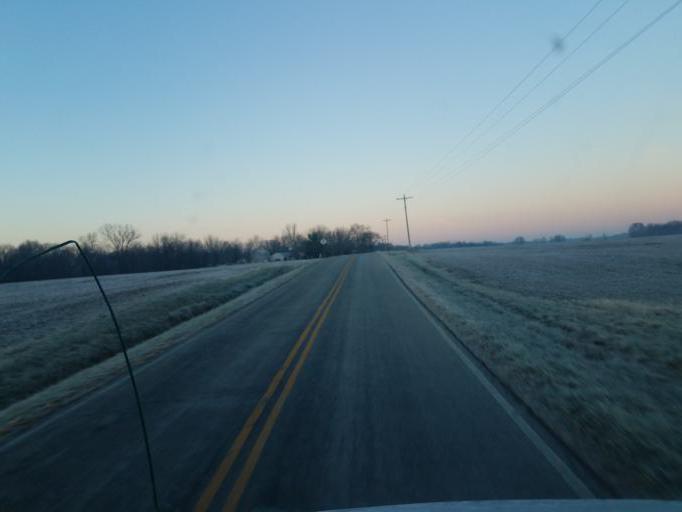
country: US
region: Ohio
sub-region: Marion County
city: Marion
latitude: 40.5187
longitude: -83.0282
